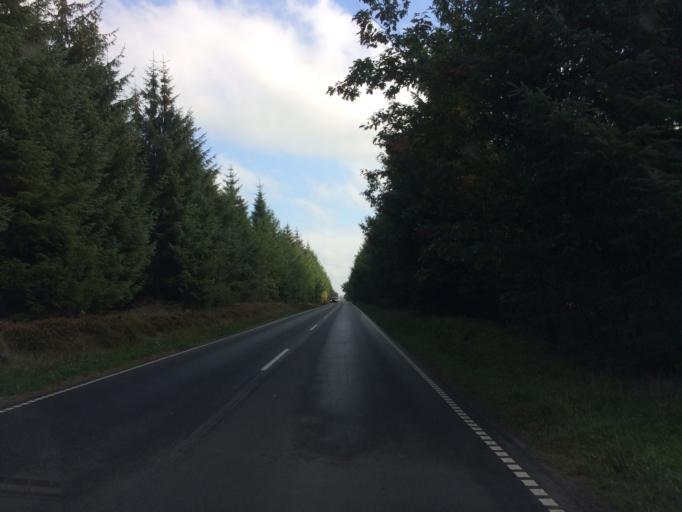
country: DK
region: Central Jutland
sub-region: Holstebro Kommune
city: Vinderup
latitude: 56.4678
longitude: 8.9132
